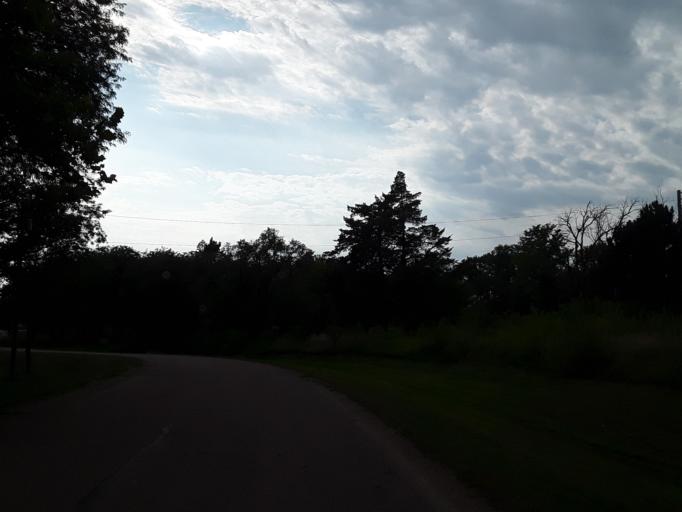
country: US
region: Nebraska
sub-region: Saunders County
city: Ashland
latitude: 41.1027
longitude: -96.4376
